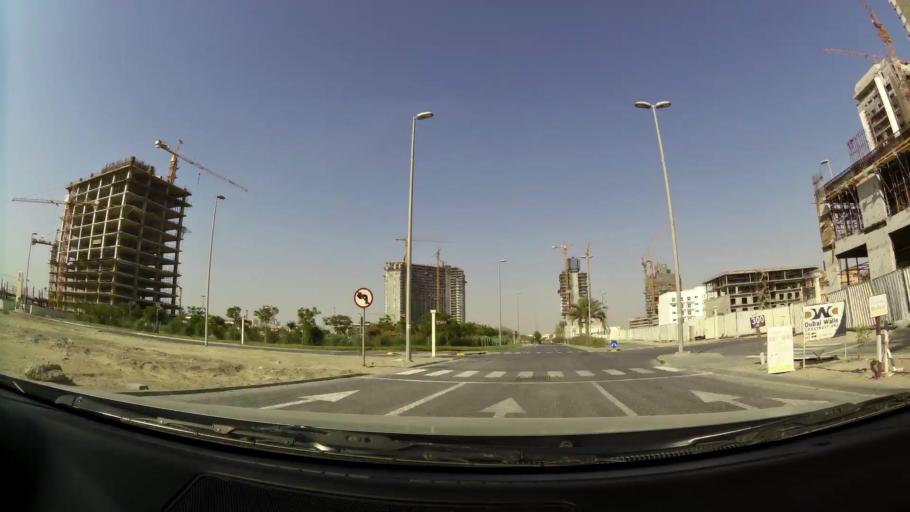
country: AE
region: Dubai
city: Dubai
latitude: 25.0537
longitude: 55.2001
